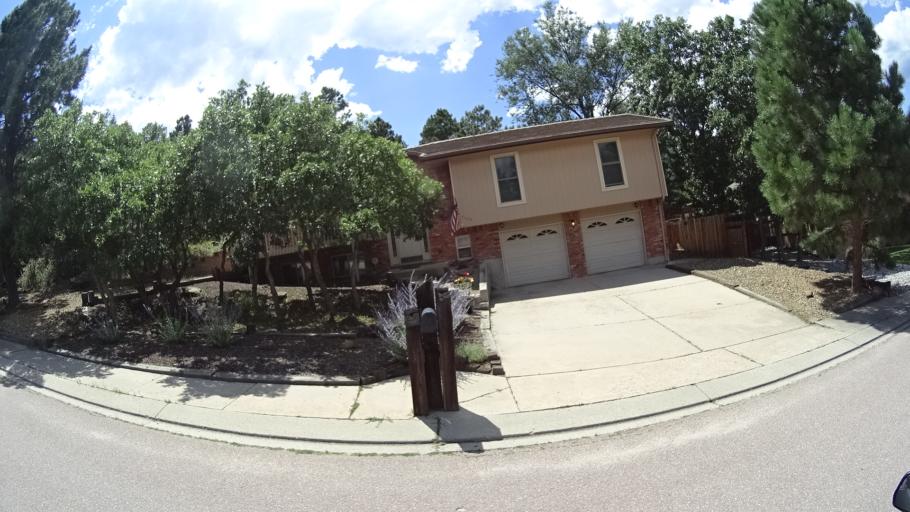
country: US
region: Colorado
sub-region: El Paso County
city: Air Force Academy
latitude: 38.9347
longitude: -104.8392
